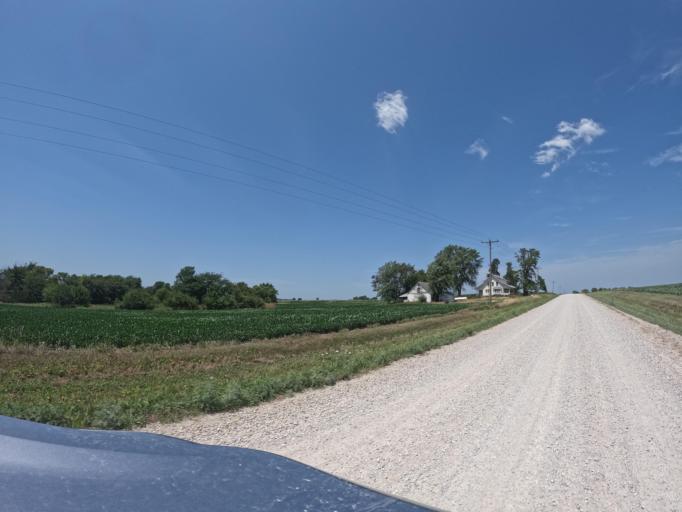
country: US
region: Iowa
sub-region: Henry County
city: Mount Pleasant
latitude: 40.9363
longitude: -91.6457
